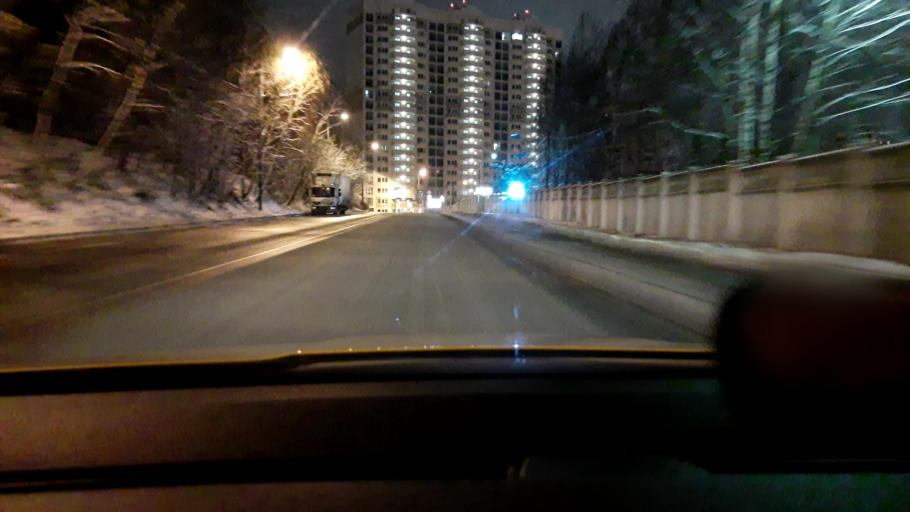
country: RU
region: Moskovskaya
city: Odintsovo
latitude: 55.6716
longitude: 37.2974
